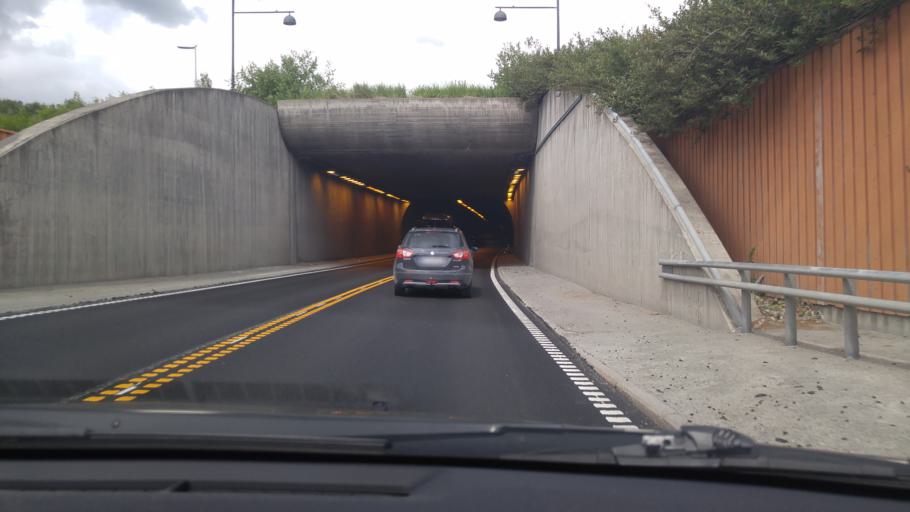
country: NO
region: Nord-Trondelag
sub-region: Steinkjer
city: Steinkjer
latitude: 64.0234
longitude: 11.4869
